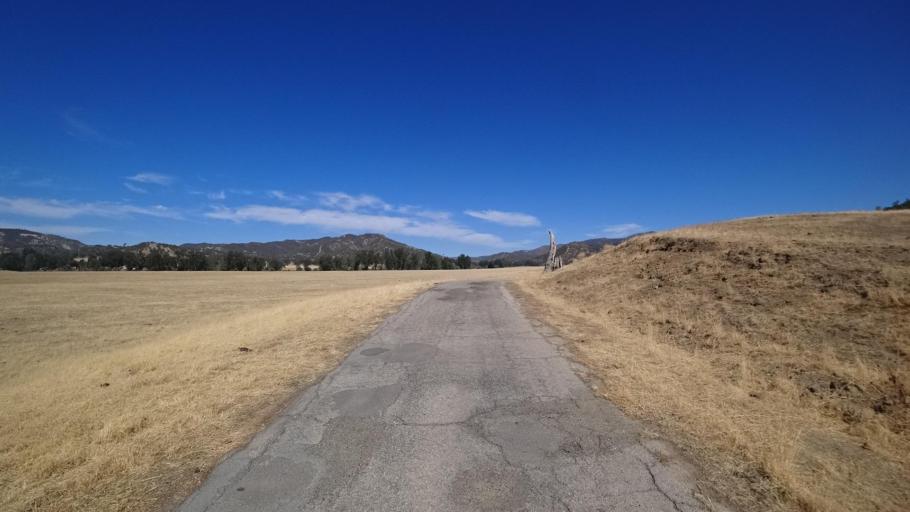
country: US
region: California
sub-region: Fresno County
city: Coalinga
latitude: 36.2002
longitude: -120.7053
